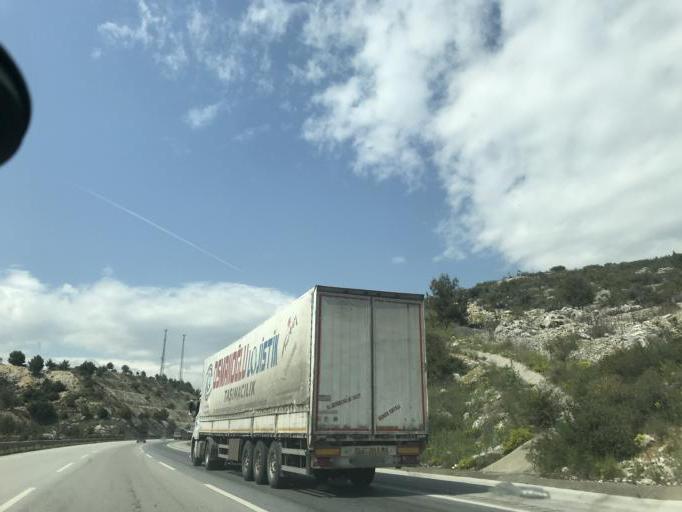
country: TR
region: Mersin
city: Tarsus
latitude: 37.1512
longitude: 34.8401
